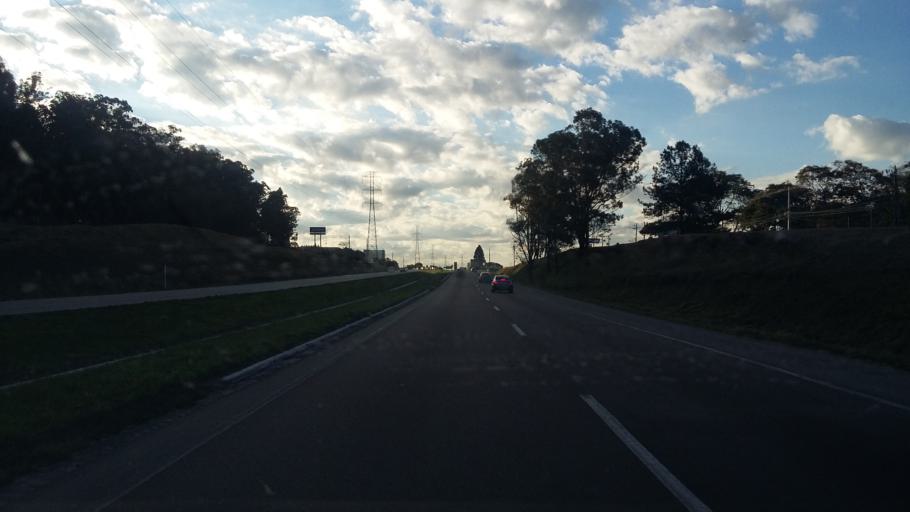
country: BR
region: Parana
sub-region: Curitiba
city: Curitiba
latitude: -25.4614
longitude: -49.3584
